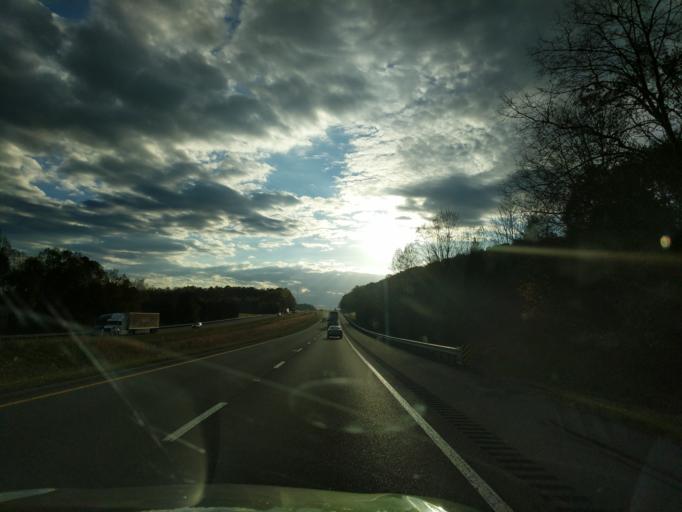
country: US
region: Tennessee
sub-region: Sullivan County
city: Blountville
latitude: 36.5518
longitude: -82.3210
